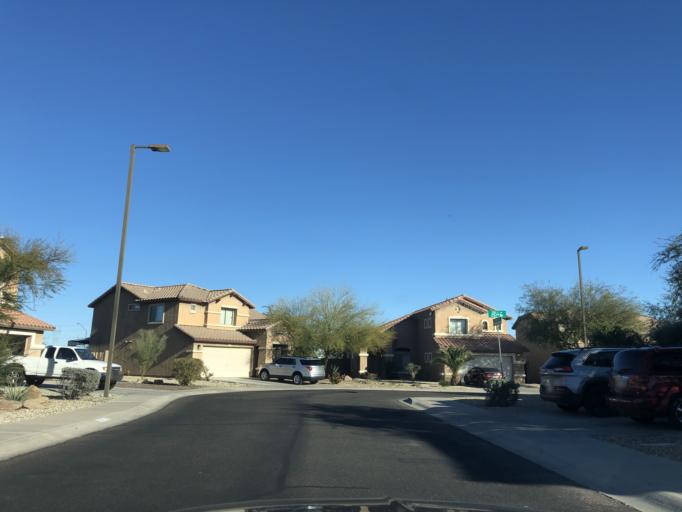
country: US
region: Arizona
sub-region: Maricopa County
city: Buckeye
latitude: 33.4274
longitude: -112.6047
